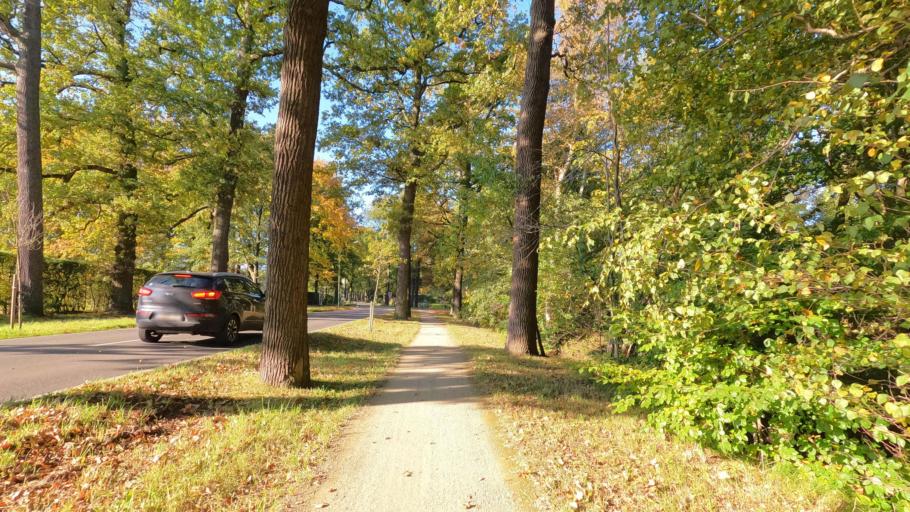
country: BE
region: Flanders
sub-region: Provincie Antwerpen
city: Schilde
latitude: 51.2641
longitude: 4.5701
